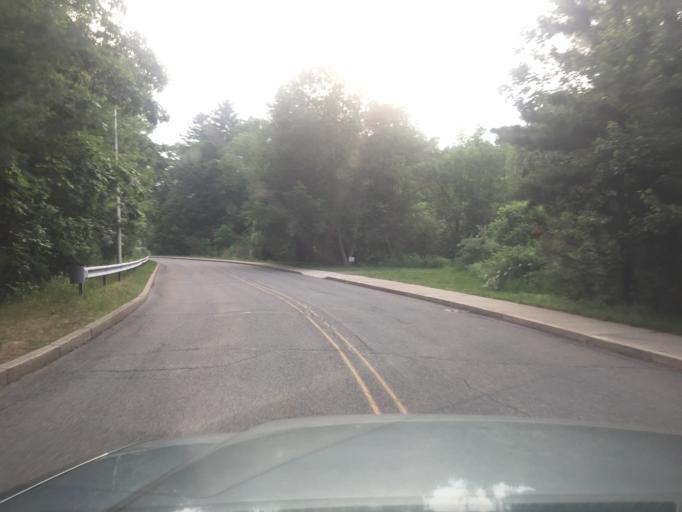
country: US
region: Massachusetts
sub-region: Norfolk County
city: Franklin
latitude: 42.0970
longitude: -71.4248
